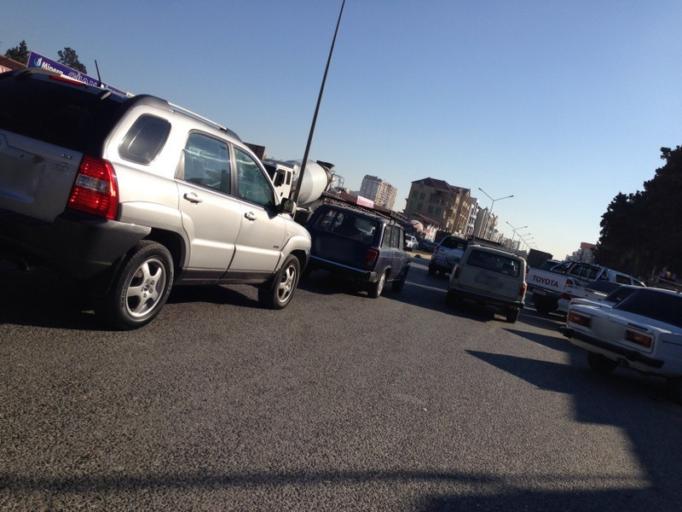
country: AZ
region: Baki
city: Baku
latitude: 40.4155
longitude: 49.8588
